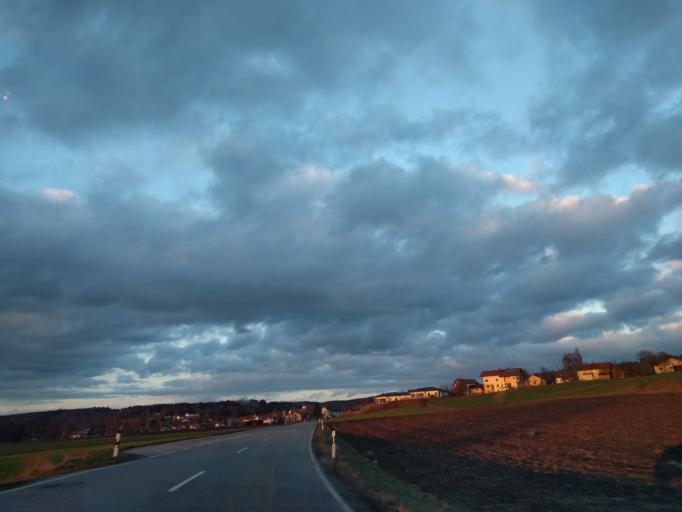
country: DE
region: Bavaria
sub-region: Lower Bavaria
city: Hofkirchen
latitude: 48.6860
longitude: 13.1167
